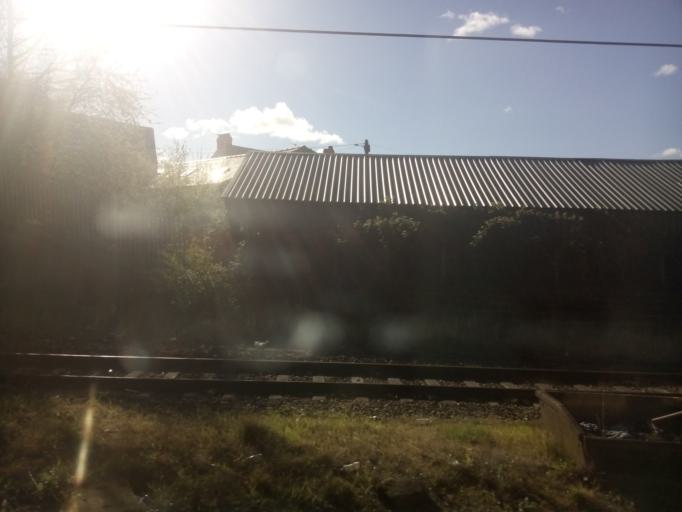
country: GB
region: England
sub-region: Darlington
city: Darlington
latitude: 54.5304
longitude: -1.5436
